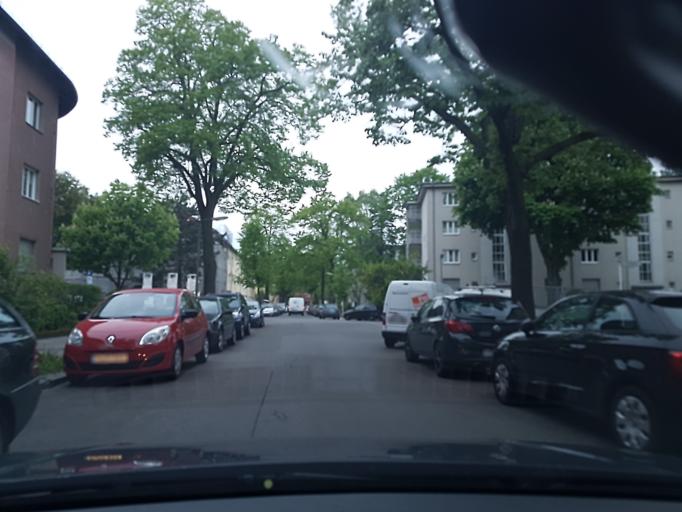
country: DE
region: Berlin
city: Mariendorf
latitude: 52.4359
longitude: 13.3829
